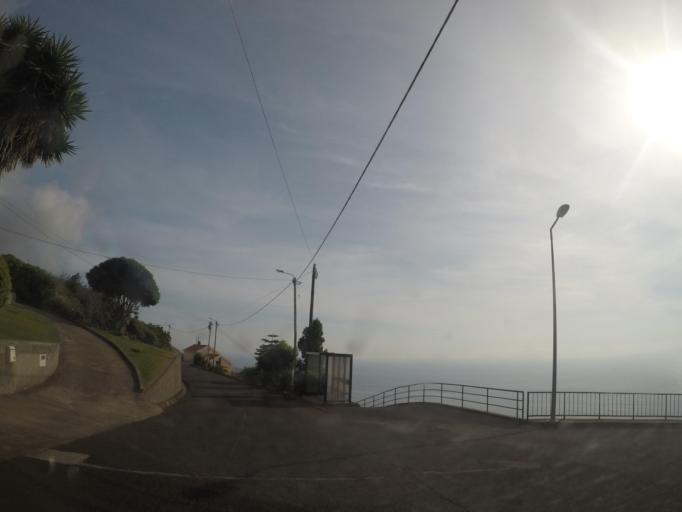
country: PT
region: Madeira
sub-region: Calheta
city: Faja da Ovelha
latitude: 32.7735
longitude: -17.2370
